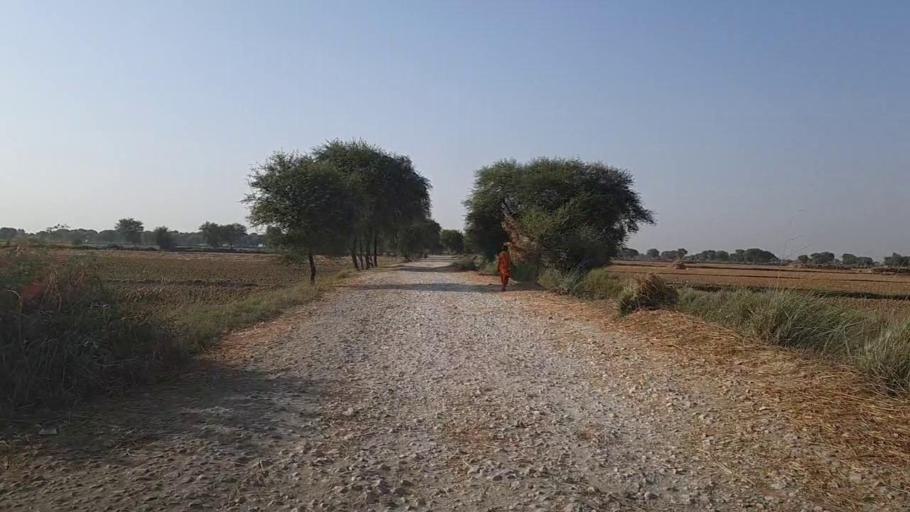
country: PK
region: Sindh
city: Kashmor
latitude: 28.4040
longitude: 69.4166
